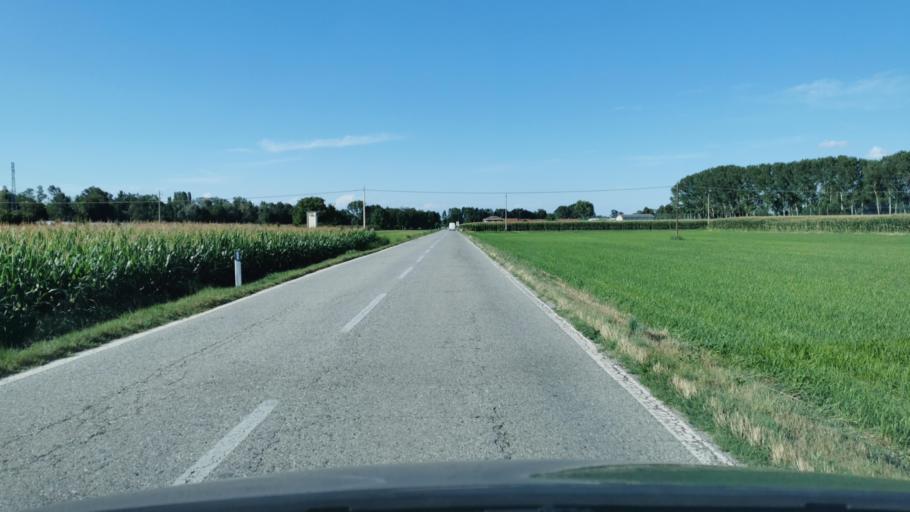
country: IT
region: Piedmont
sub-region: Provincia di Cuneo
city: Genola
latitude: 44.6036
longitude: 7.6224
